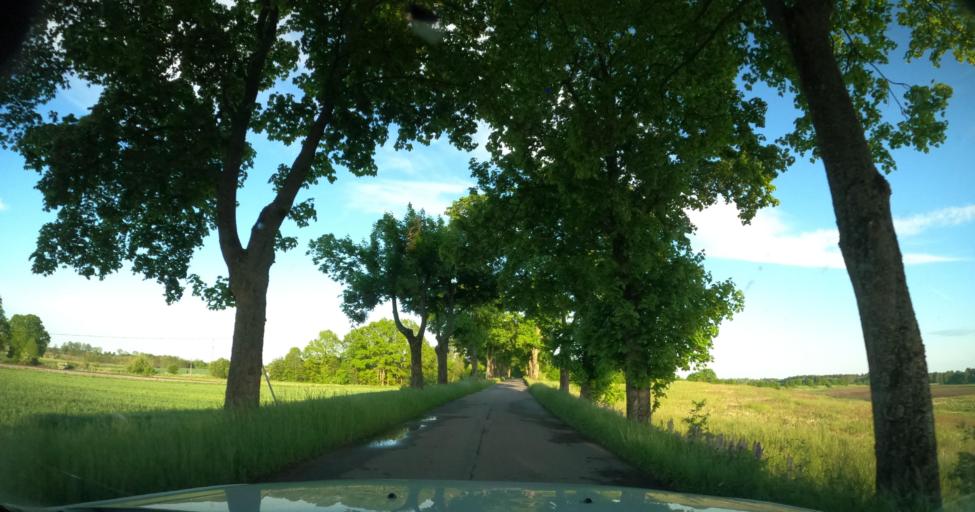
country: PL
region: Warmian-Masurian Voivodeship
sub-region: Powiat lidzbarski
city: Orneta
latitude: 54.1760
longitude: 20.1420
